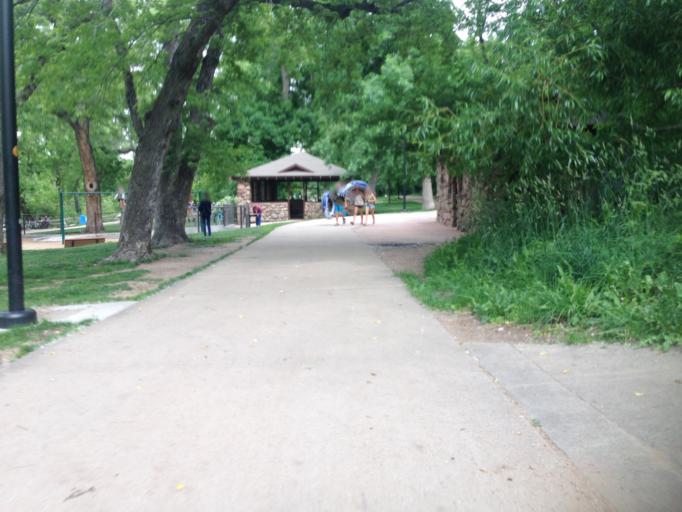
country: US
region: Colorado
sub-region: Boulder County
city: Boulder
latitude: 40.0129
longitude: -105.2964
